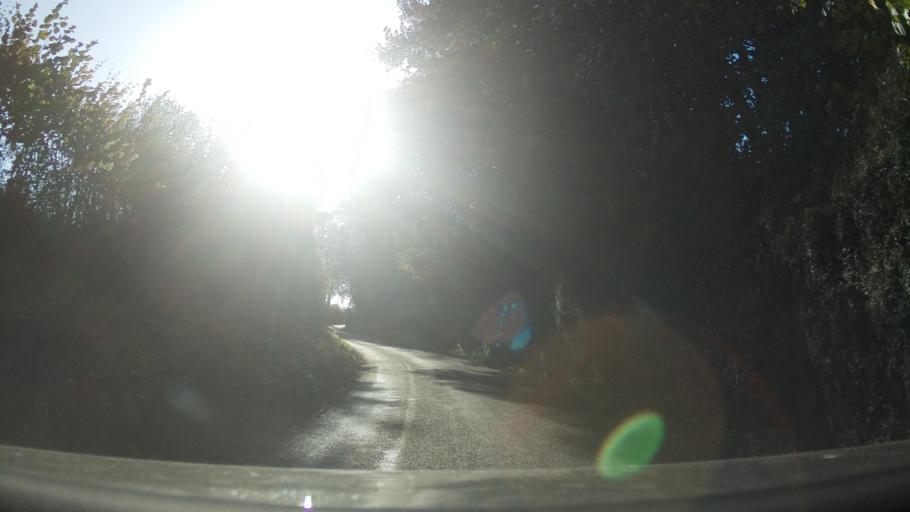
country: GB
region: England
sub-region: Somerset
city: Castle Cary
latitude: 51.0343
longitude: -2.4977
